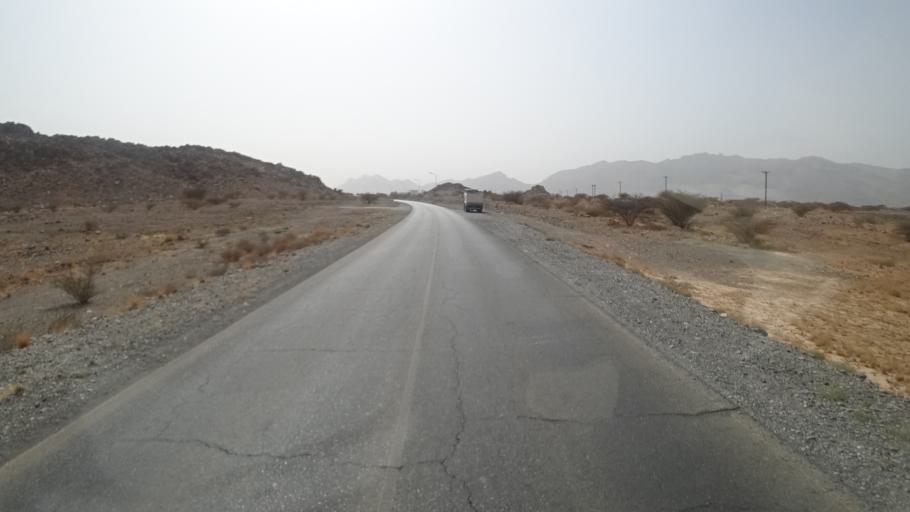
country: OM
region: Muhafazat ad Dakhiliyah
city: Nizwa
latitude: 22.9258
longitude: 57.6252
